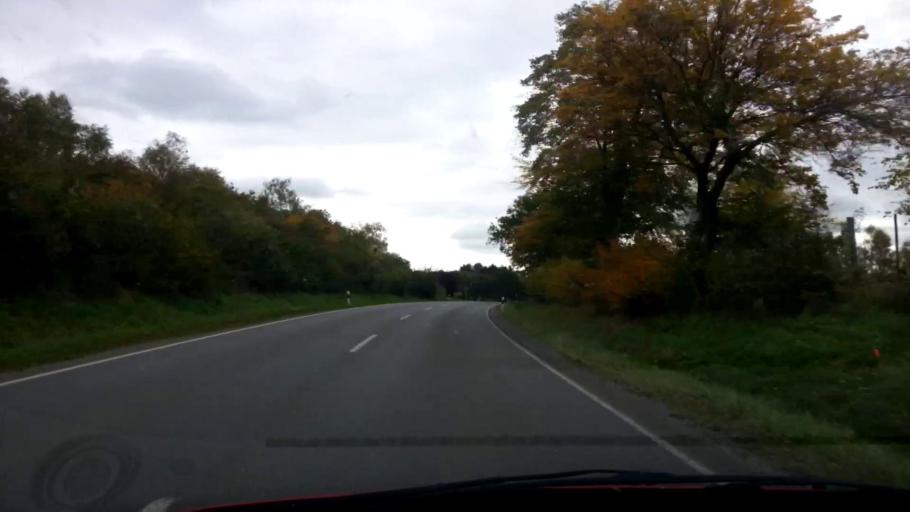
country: DE
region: Bavaria
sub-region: Upper Franconia
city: Reuth
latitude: 49.9597
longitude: 11.7020
